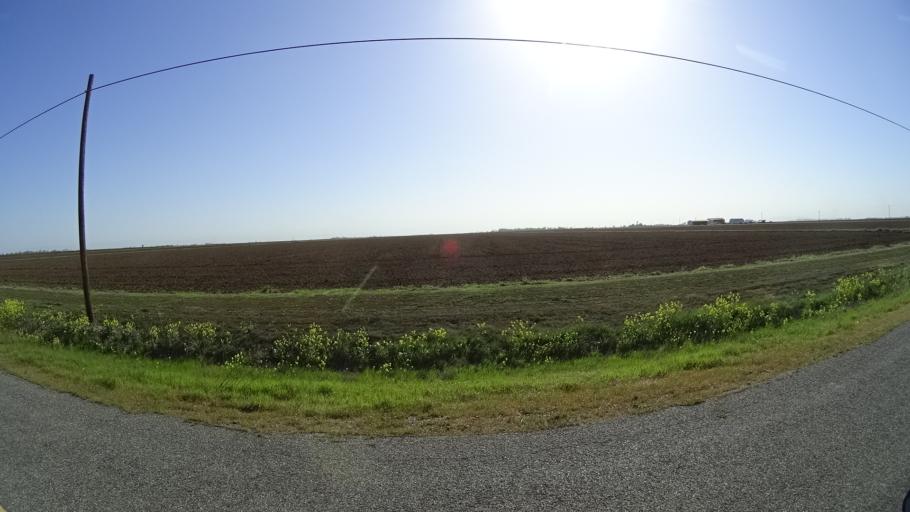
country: US
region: California
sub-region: Glenn County
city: Willows
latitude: 39.4975
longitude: -122.1745
